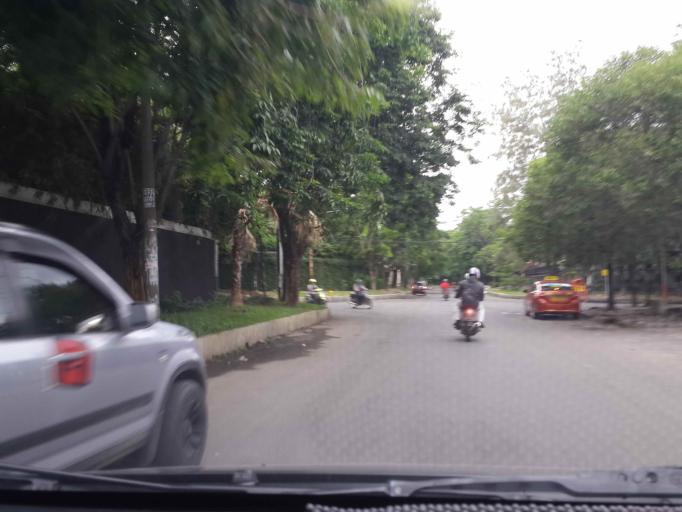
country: ID
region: East Java
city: Gubengairlangga
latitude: -7.2804
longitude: 112.7324
